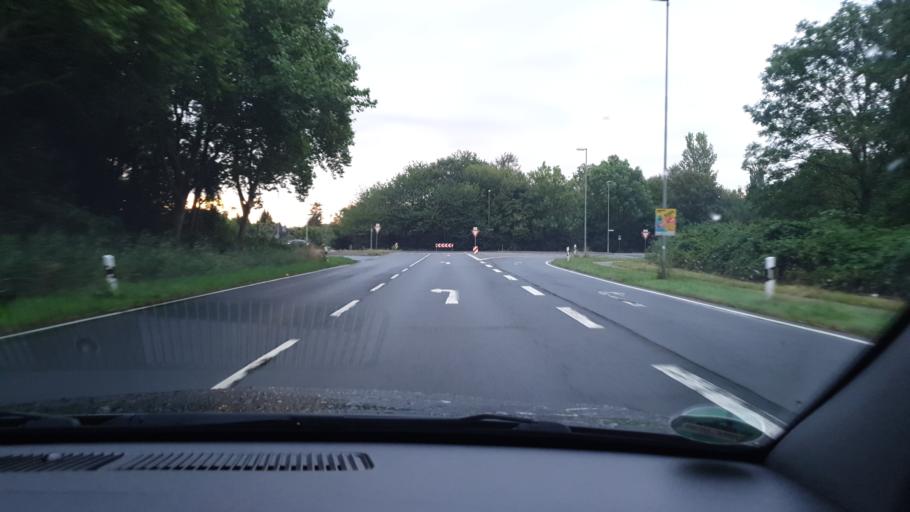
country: DE
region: Lower Saxony
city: Wilhelmshaven
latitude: 53.5371
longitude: 8.1152
